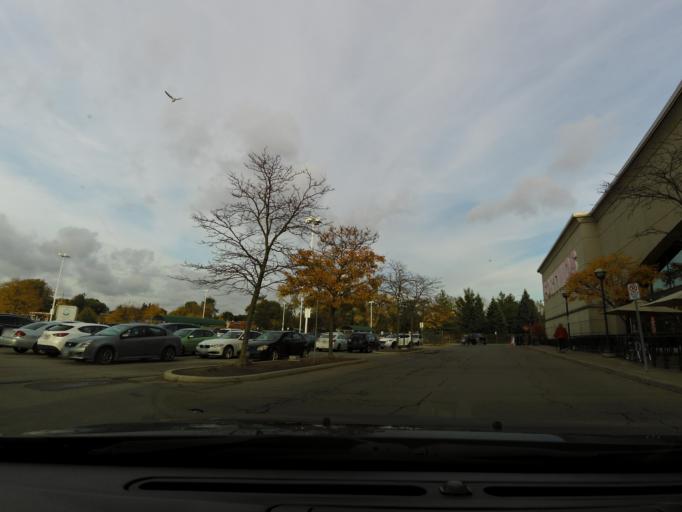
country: CA
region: Ontario
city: Ancaster
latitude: 43.2557
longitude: -79.9291
